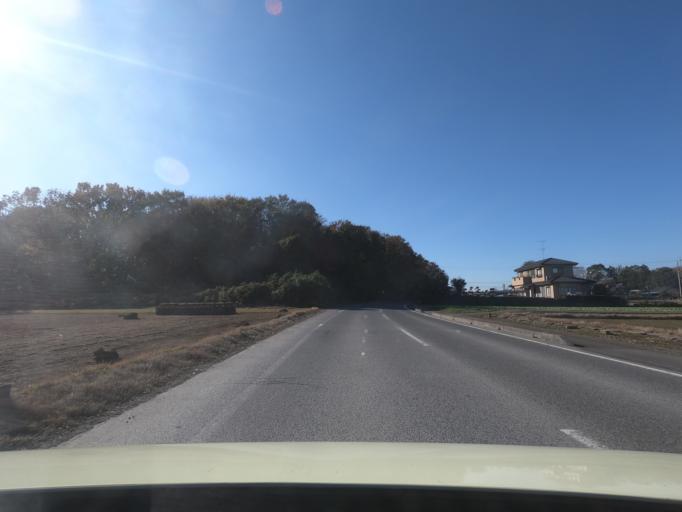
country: JP
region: Ibaraki
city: Ishige
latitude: 36.1195
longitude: 140.0534
